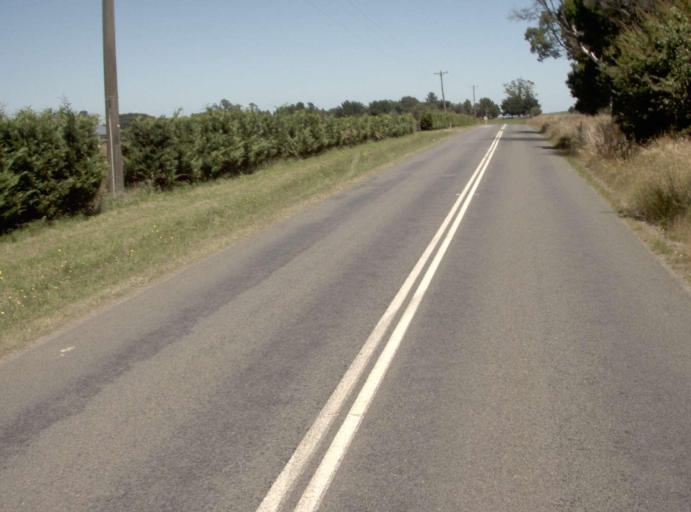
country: AU
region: Victoria
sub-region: Baw Baw
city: Warragul
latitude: -37.9462
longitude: 145.9564
